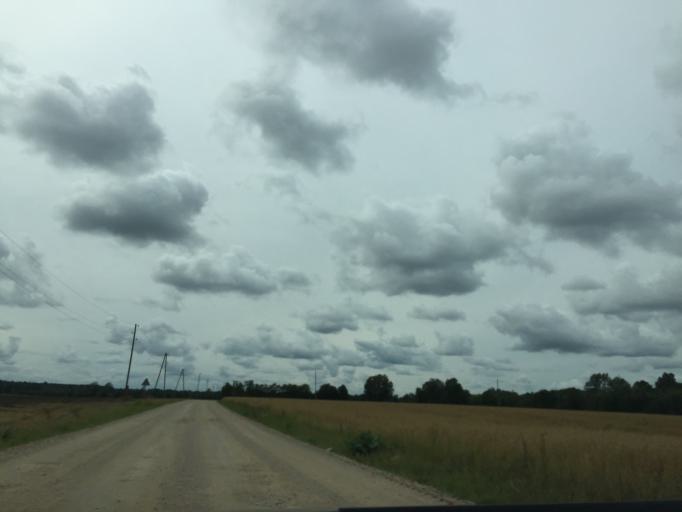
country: LV
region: Ogre
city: Jumprava
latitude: 56.7628
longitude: 24.9272
